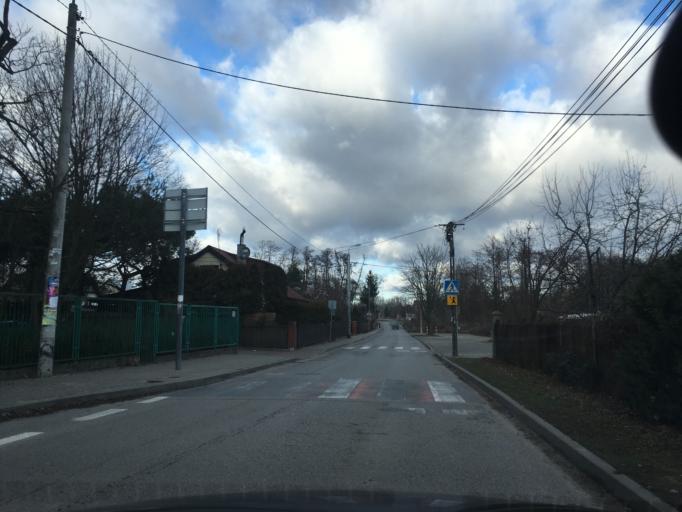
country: PL
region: Masovian Voivodeship
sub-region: Powiat piaseczynski
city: Lesznowola
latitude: 52.0371
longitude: 20.9439
